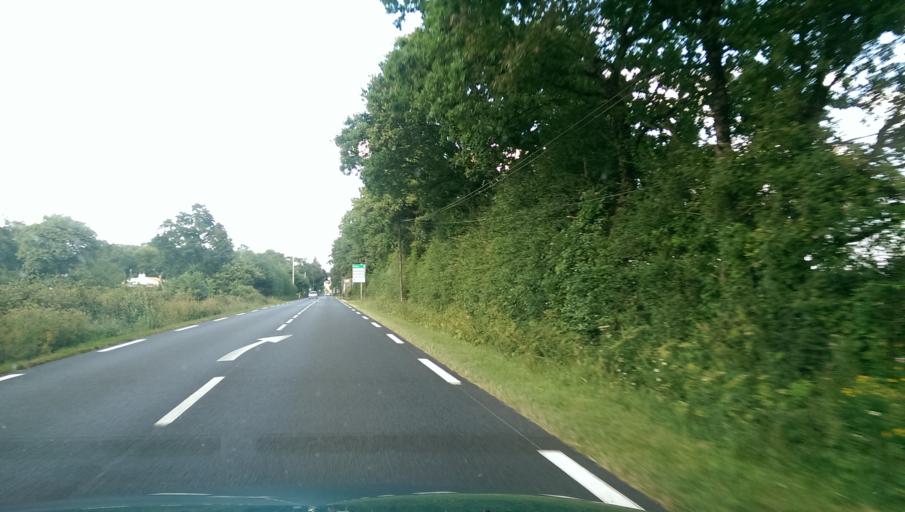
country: FR
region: Pays de la Loire
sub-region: Departement de la Vendee
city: Rocheserviere
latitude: 46.9235
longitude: -1.5320
